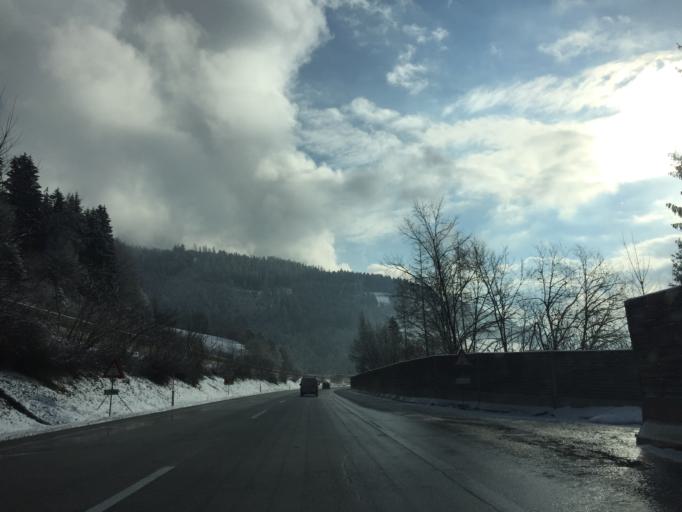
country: AT
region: Salzburg
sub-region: Politischer Bezirk Sankt Johann im Pongau
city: Huttau
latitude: 47.4300
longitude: 13.2879
